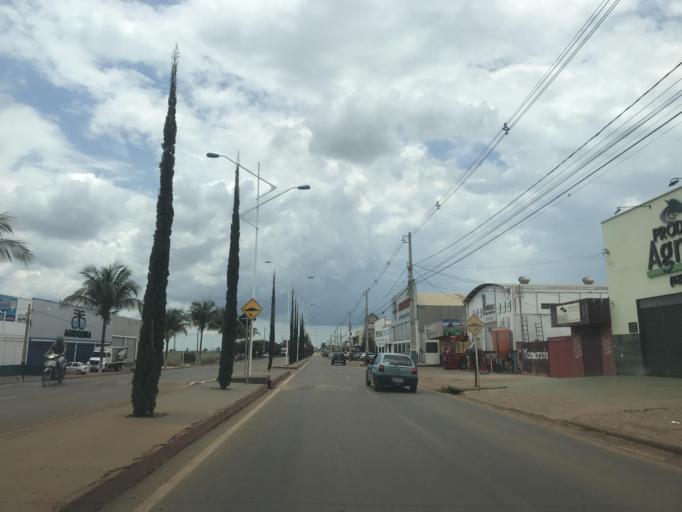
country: BR
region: Goias
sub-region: Vianopolis
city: Vianopolis
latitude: -16.7562
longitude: -48.5200
